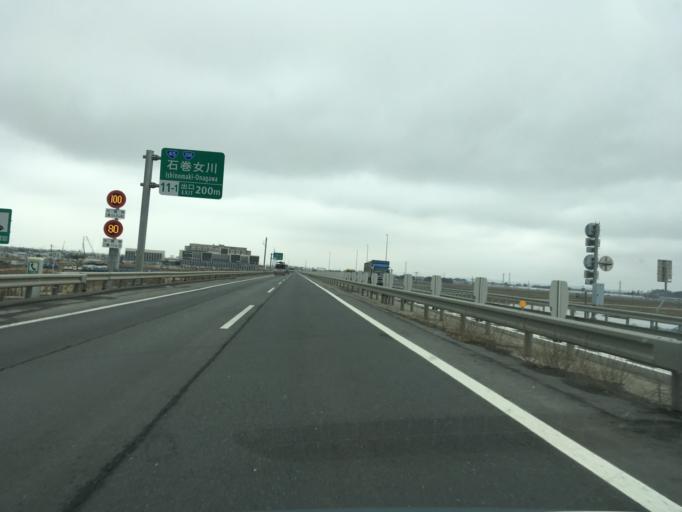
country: JP
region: Miyagi
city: Ishinomaki
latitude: 38.4619
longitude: 141.2877
